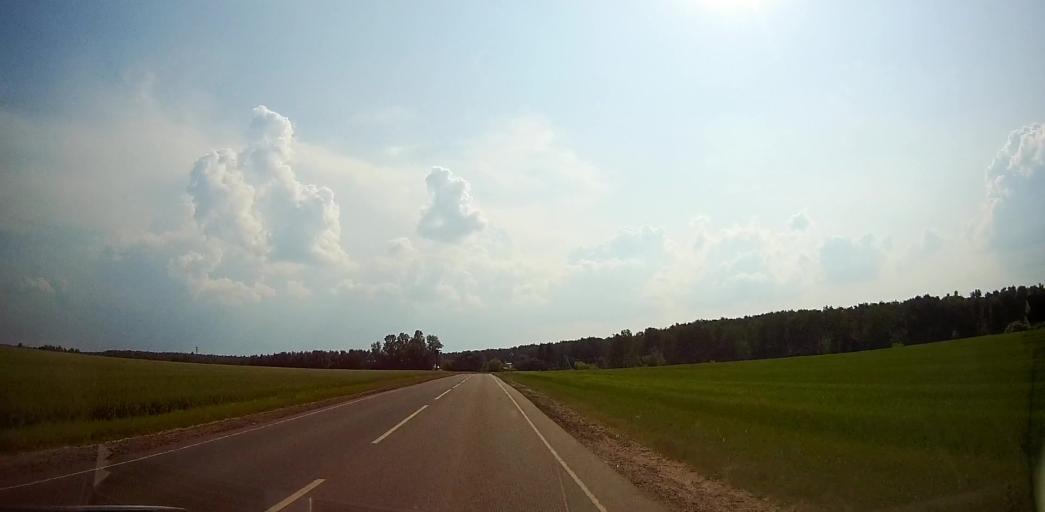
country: RU
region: Moskovskaya
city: Il'inskoye
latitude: 55.2872
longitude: 37.9385
